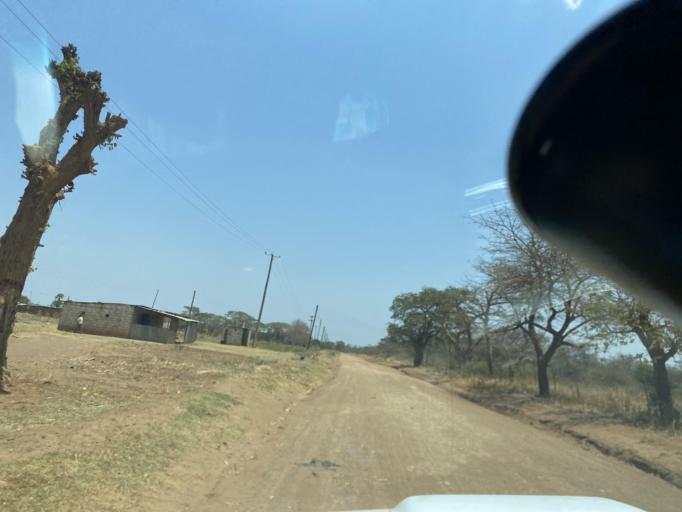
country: ZM
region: Lusaka
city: Lusaka
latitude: -15.4299
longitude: 28.0862
